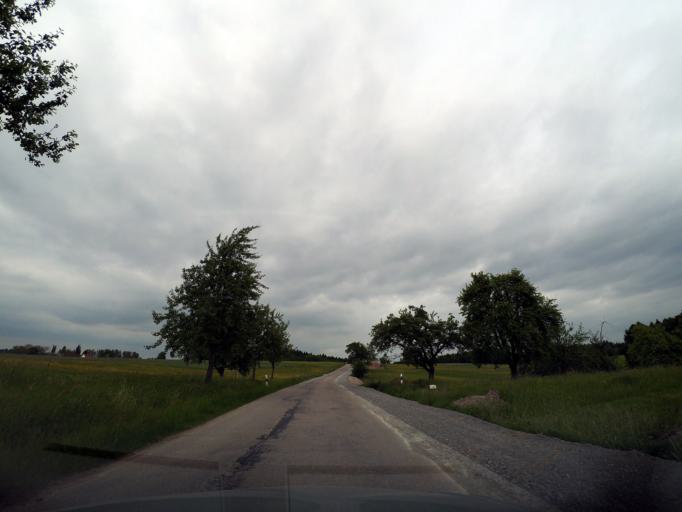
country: DE
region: Baden-Wuerttemberg
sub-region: Regierungsbezirk Stuttgart
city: Oberrot
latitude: 49.0303
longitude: 9.6850
